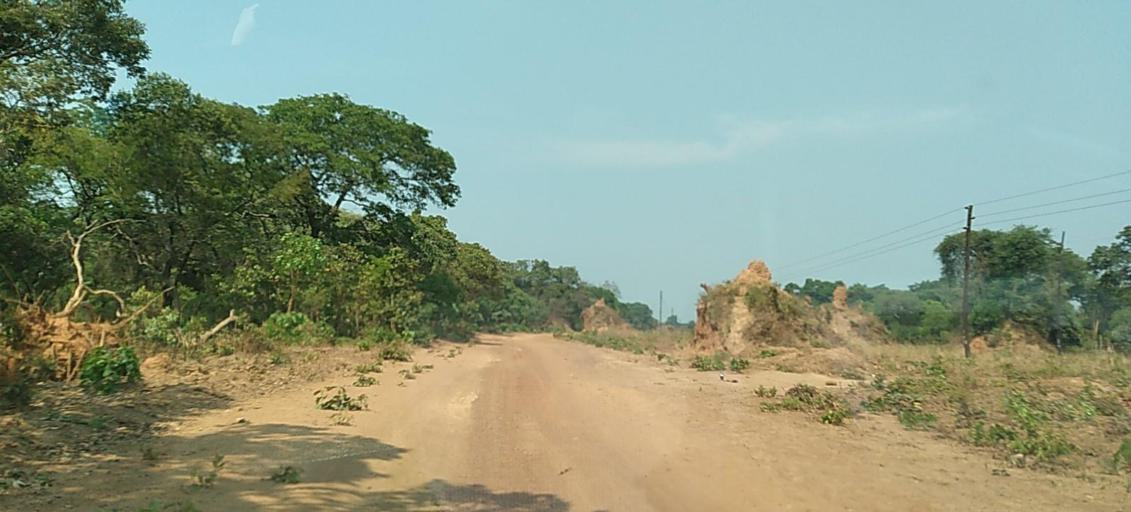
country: ZM
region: Copperbelt
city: Chingola
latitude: -13.0429
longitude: 27.4413
